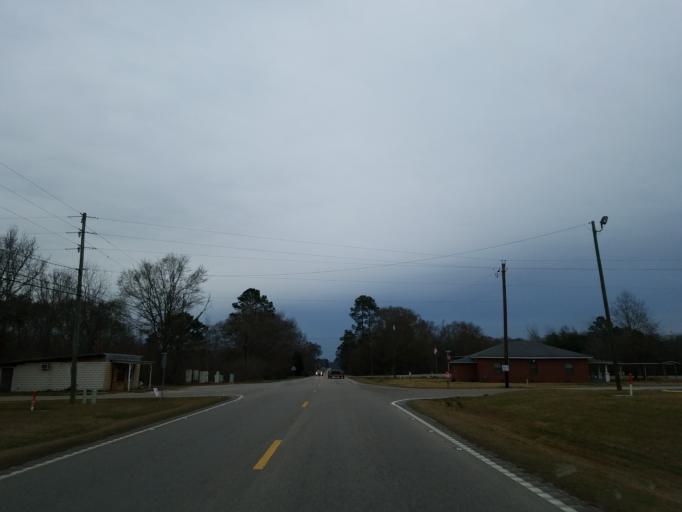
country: US
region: Mississippi
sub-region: Forrest County
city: Glendale
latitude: 31.4955
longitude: -89.2810
